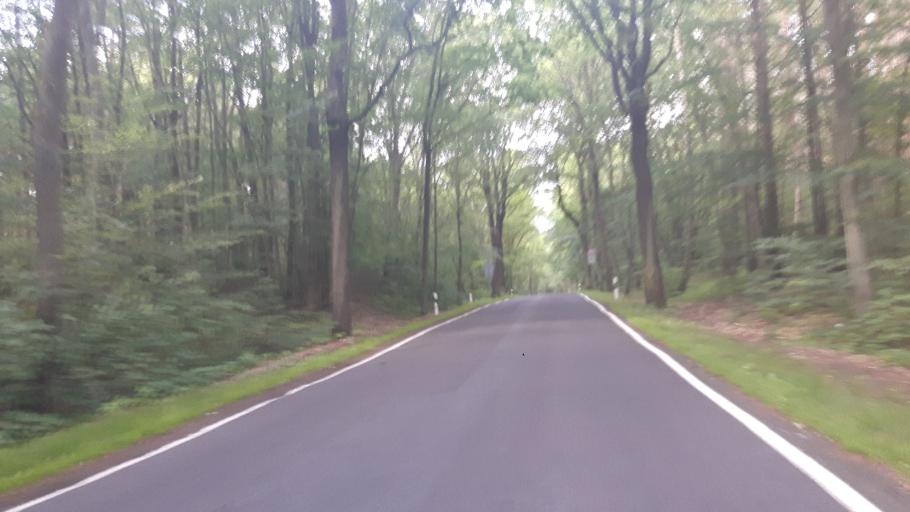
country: DE
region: Brandenburg
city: Hohenfinow
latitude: 52.7887
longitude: 13.9002
